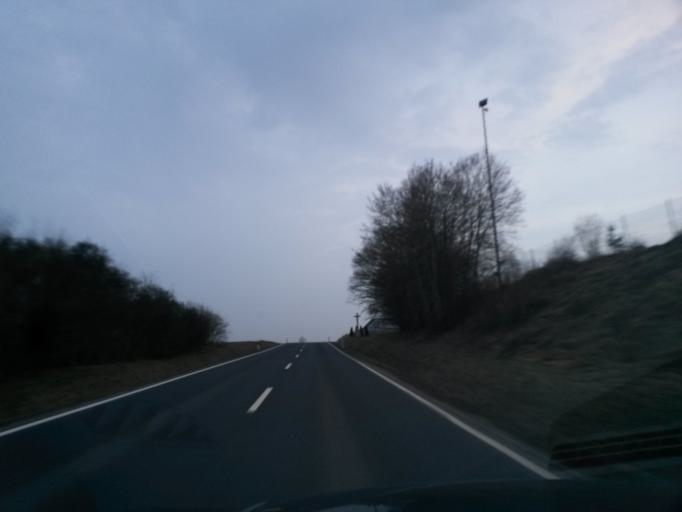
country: DE
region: Bavaria
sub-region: Regierungsbezirk Unterfranken
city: Sulzfeld
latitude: 50.2555
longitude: 10.4008
